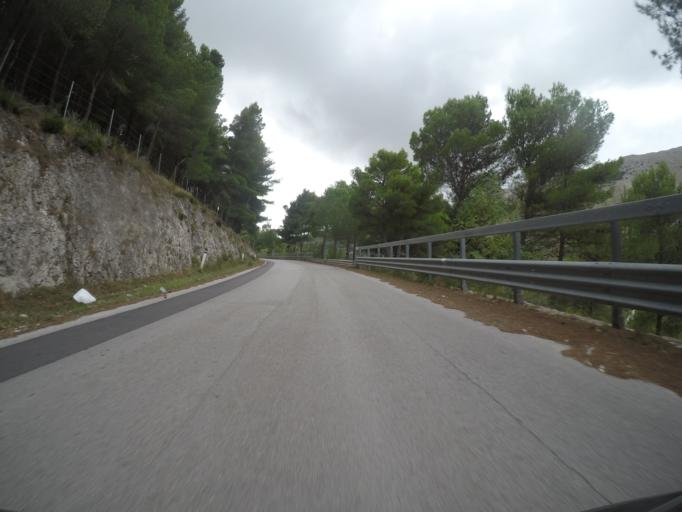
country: IT
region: Sicily
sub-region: Palermo
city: Montelepre
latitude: 38.1155
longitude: 13.1669
